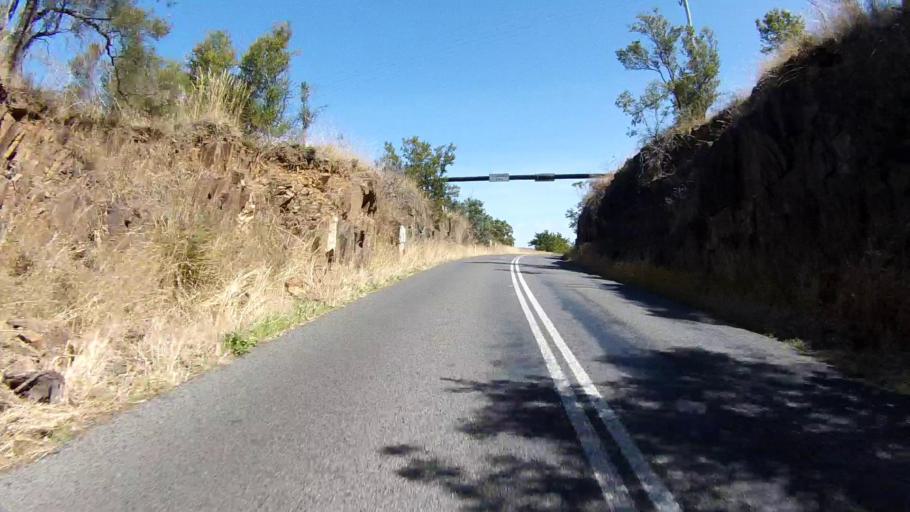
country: AU
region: Tasmania
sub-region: Sorell
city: Sorell
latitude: -42.4909
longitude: 147.9331
